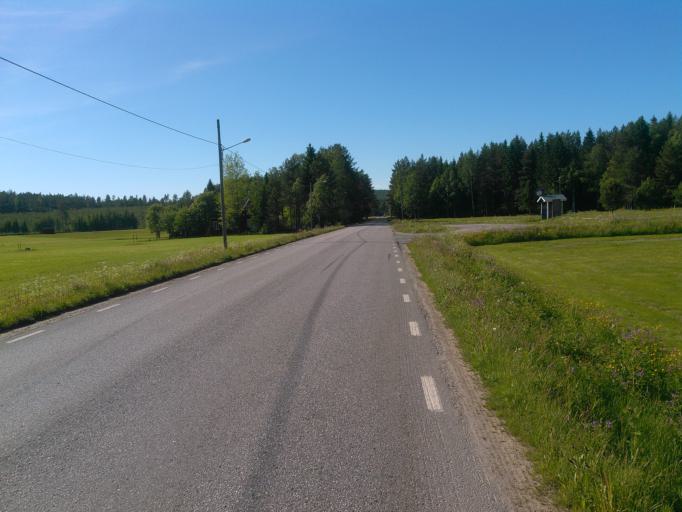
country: SE
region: Vaesterbotten
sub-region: Umea Kommun
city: Roback
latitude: 63.8299
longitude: 20.1137
